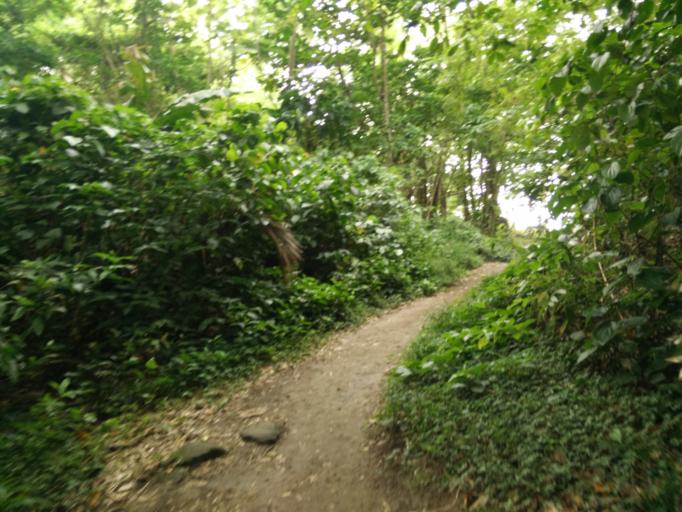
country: MQ
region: Martinique
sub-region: Martinique
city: Saint-Pierre
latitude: 14.8417
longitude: -61.2188
